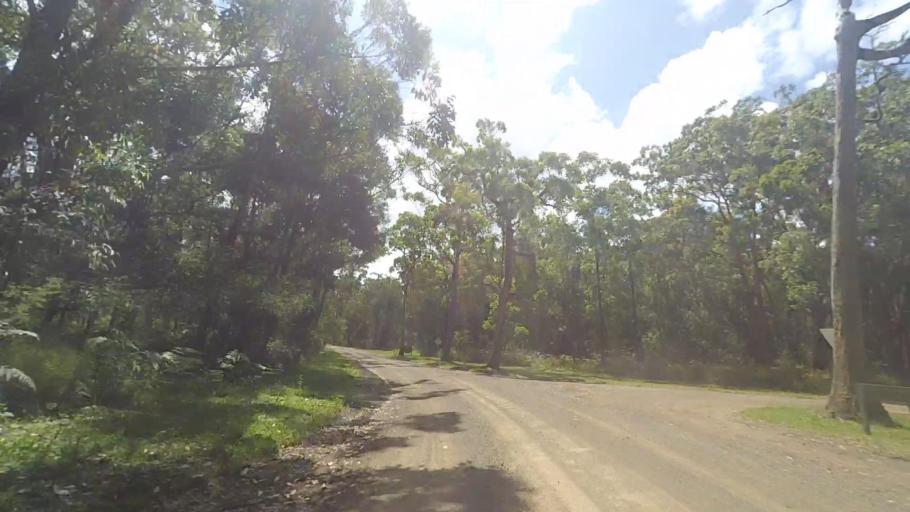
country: AU
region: New South Wales
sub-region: Great Lakes
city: Bulahdelah
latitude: -32.4896
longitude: 152.2743
